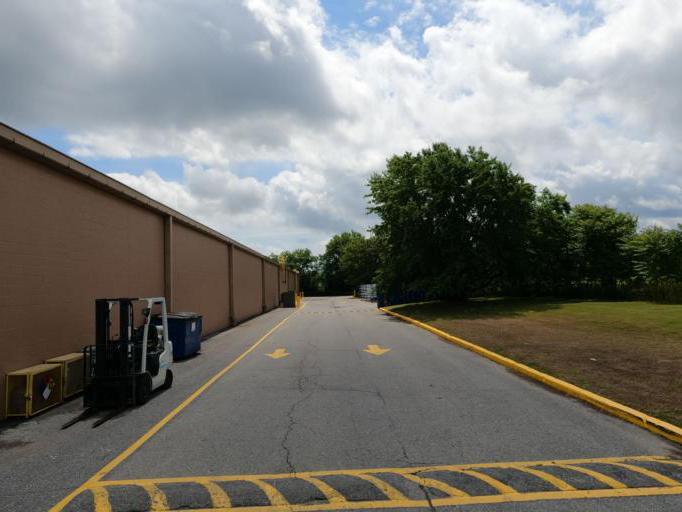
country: US
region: Delaware
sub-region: Sussex County
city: Lewes
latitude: 38.7274
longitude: -75.1332
